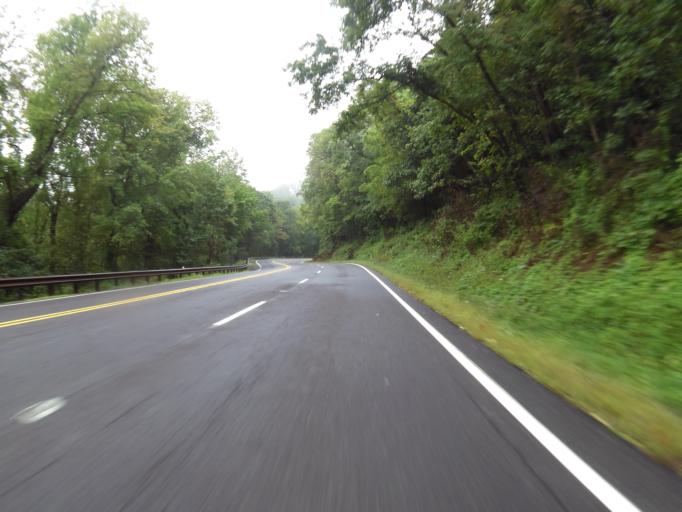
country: US
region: Virginia
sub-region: Rappahannock County
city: Washington
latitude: 38.6619
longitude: -78.3049
